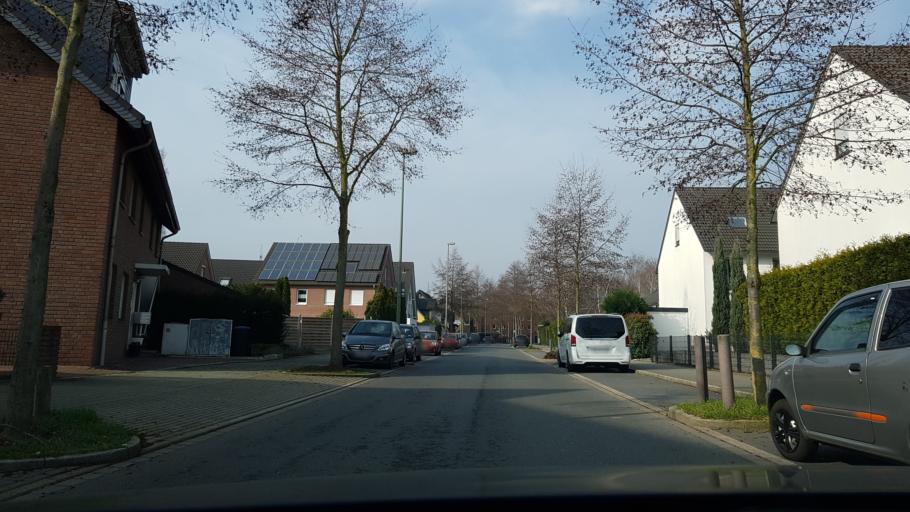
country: DE
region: North Rhine-Westphalia
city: Meiderich
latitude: 51.5111
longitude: 6.7937
